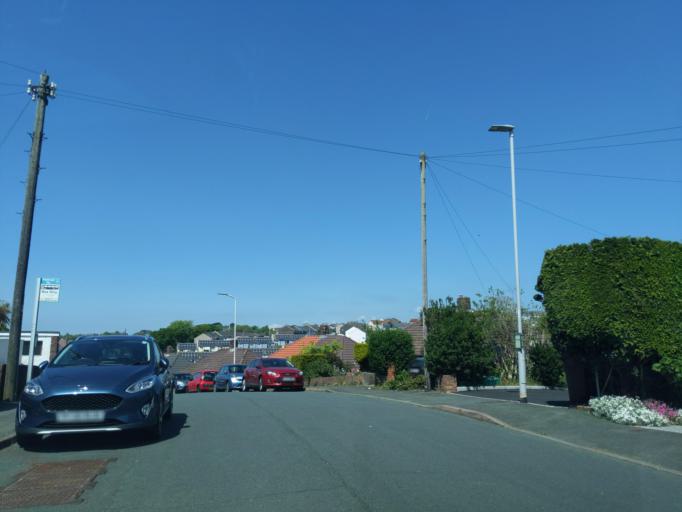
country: GB
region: England
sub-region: Cornwall
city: Torpoint
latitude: 50.4016
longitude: -4.1755
